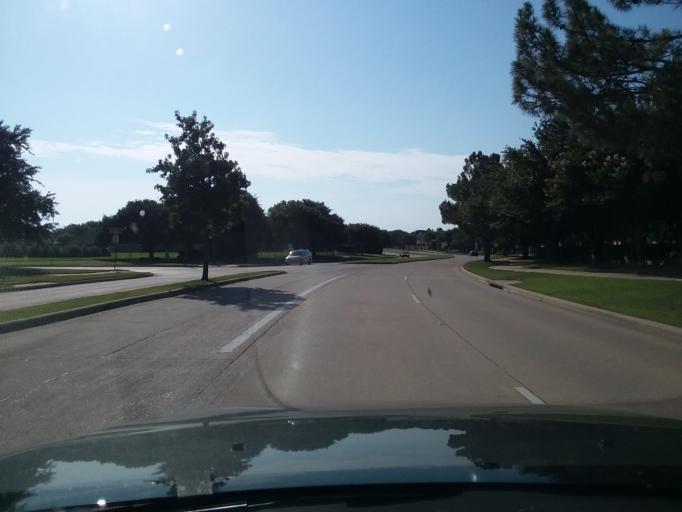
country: US
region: Texas
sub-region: Denton County
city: Highland Village
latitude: 33.0662
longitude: -97.0525
